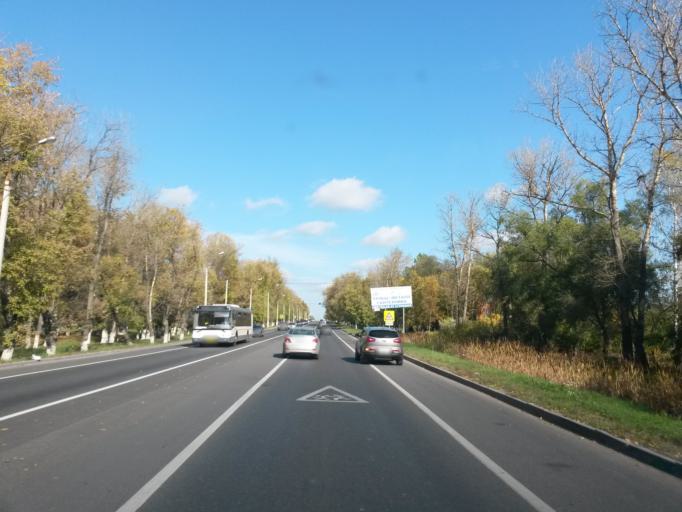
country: RU
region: Moskovskaya
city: L'vovskiy
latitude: 55.3169
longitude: 37.5287
